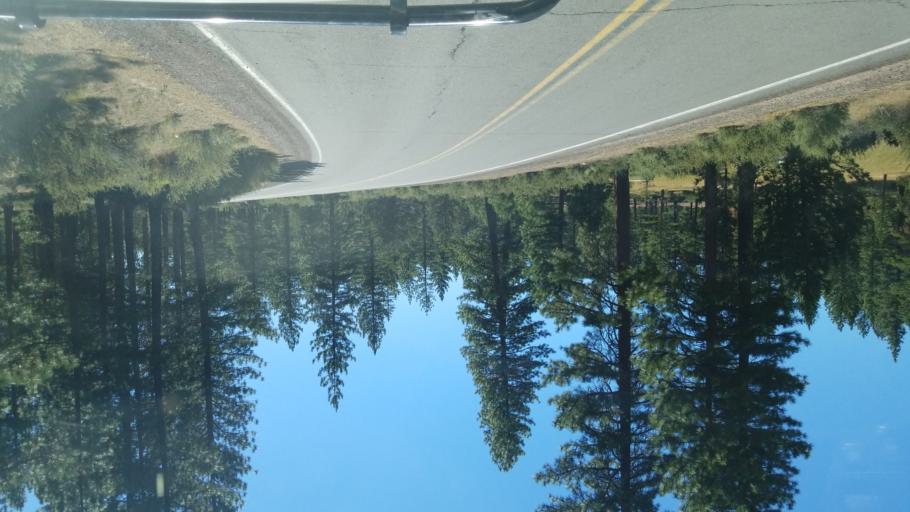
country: US
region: California
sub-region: Lassen County
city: Susanville
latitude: 40.4227
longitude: -120.7141
